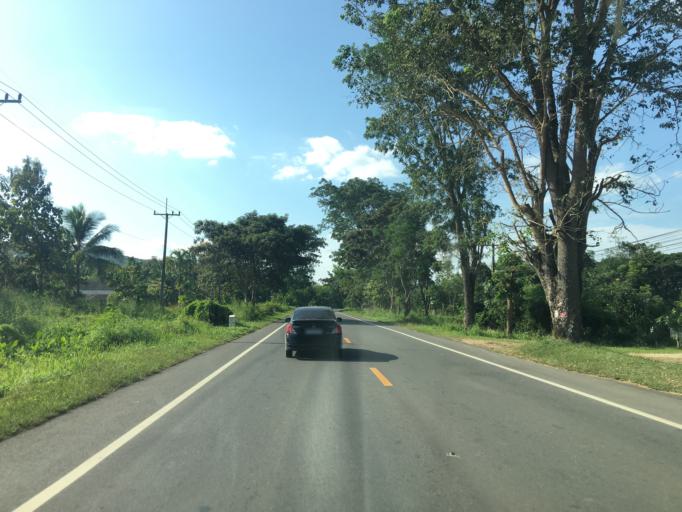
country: TH
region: Phayao
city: Chun
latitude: 19.3539
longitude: 100.1008
